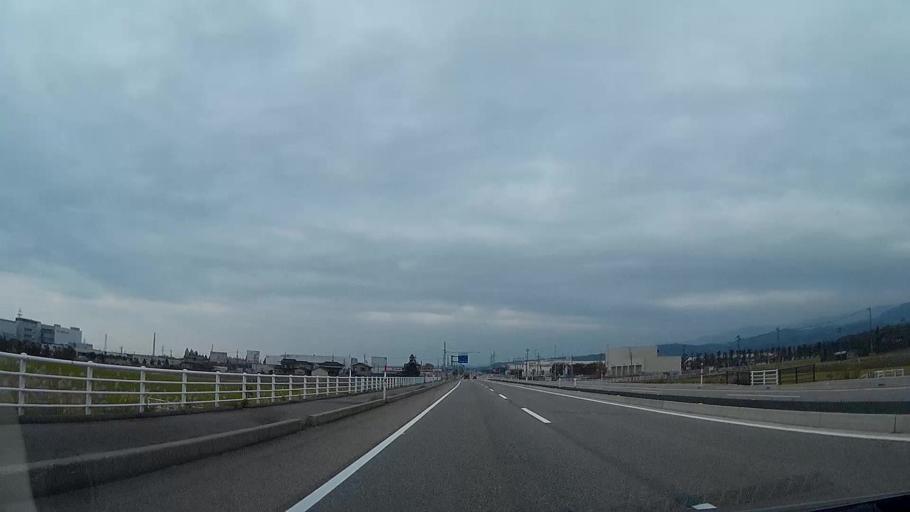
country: JP
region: Toyama
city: Uozu
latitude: 36.7749
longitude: 137.3888
